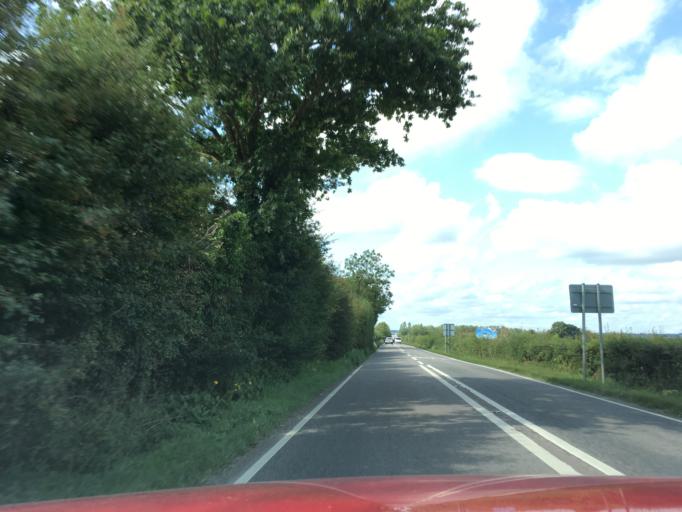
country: GB
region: England
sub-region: Kent
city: Headcorn
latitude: 51.1561
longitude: 0.6349
